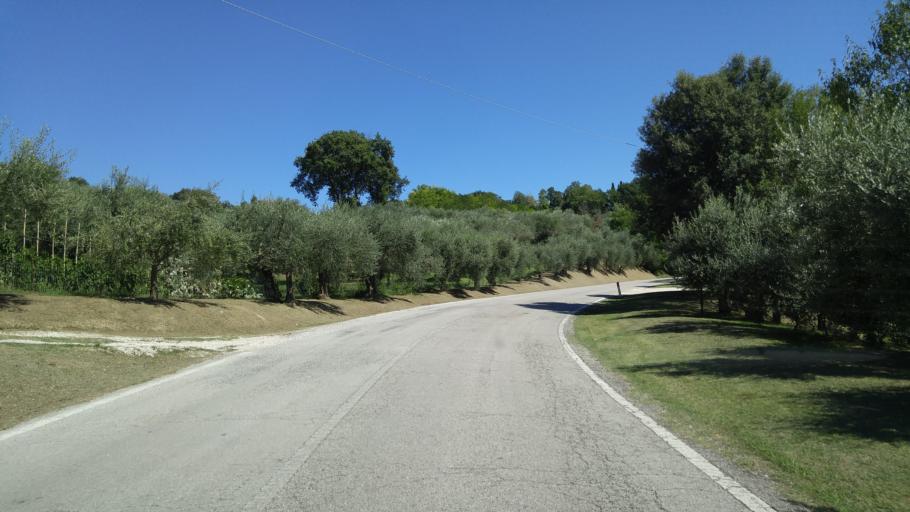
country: IT
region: The Marches
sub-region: Provincia di Pesaro e Urbino
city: Cartoceto
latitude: 43.7616
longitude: 12.8878
